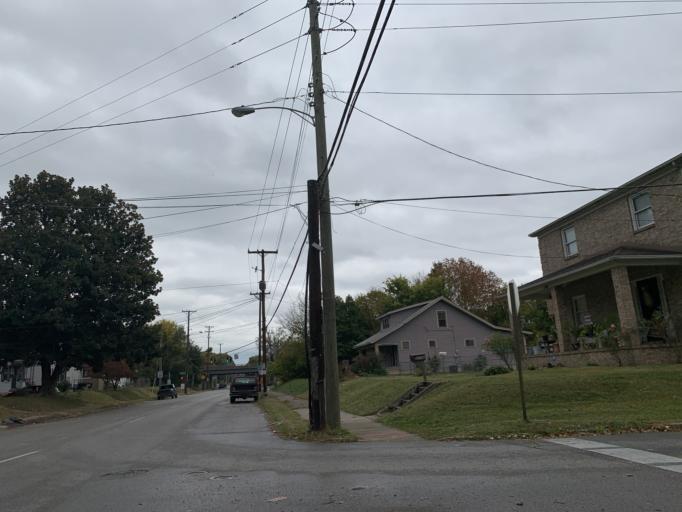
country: US
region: Indiana
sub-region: Floyd County
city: New Albany
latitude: 38.2719
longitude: -85.8108
